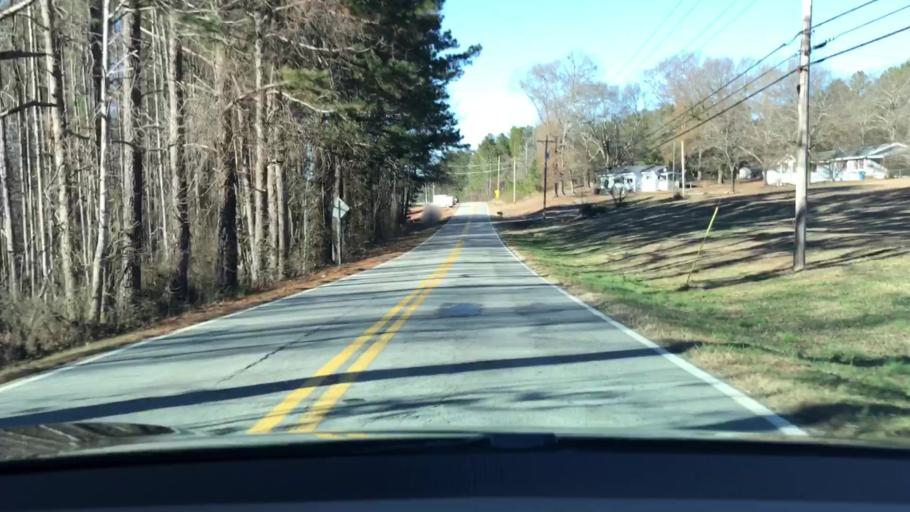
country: US
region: Georgia
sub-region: Barrow County
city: Auburn
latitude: 34.0446
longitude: -83.8440
